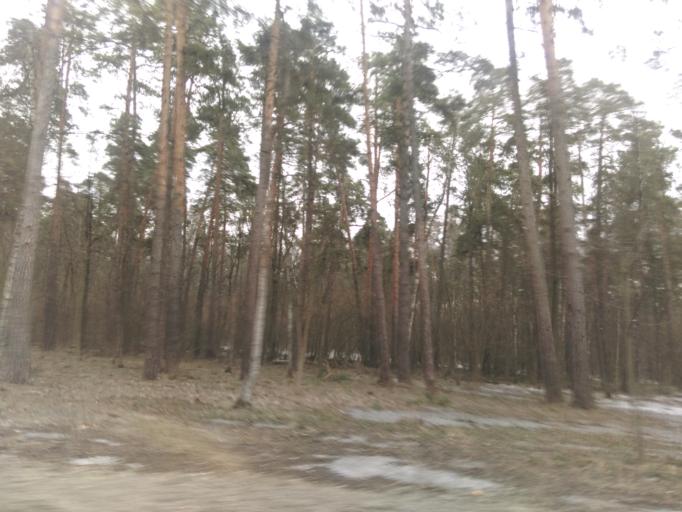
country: RU
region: Moskovskaya
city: Nemchinovka
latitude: 55.7513
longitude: 37.3325
